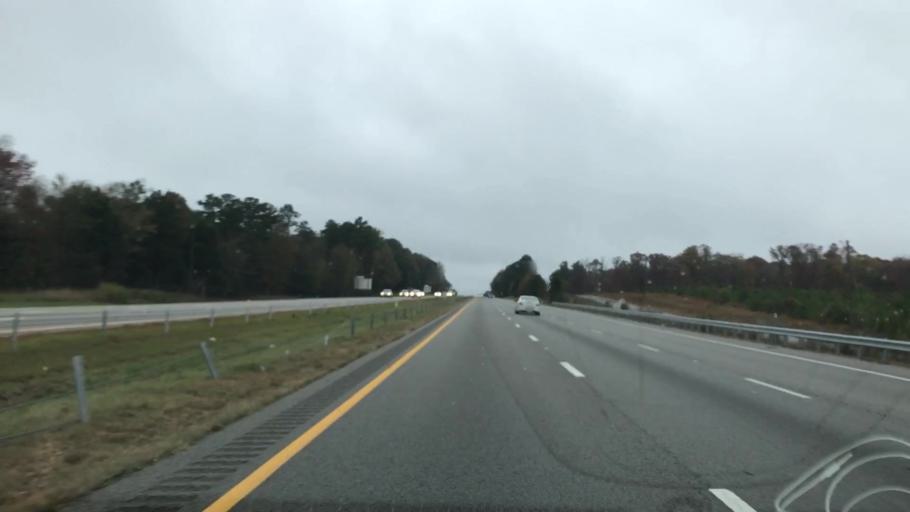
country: US
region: South Carolina
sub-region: Newberry County
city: Newberry
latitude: 34.2957
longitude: -81.5493
